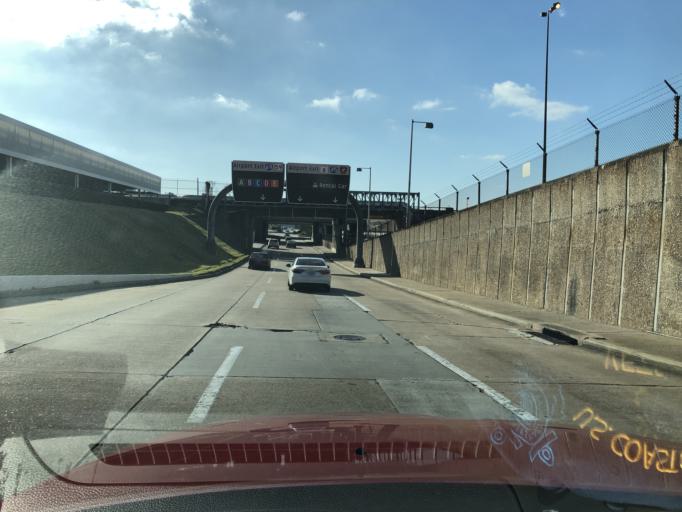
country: US
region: Texas
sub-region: Harris County
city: Aldine
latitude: 29.9853
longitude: -95.3428
